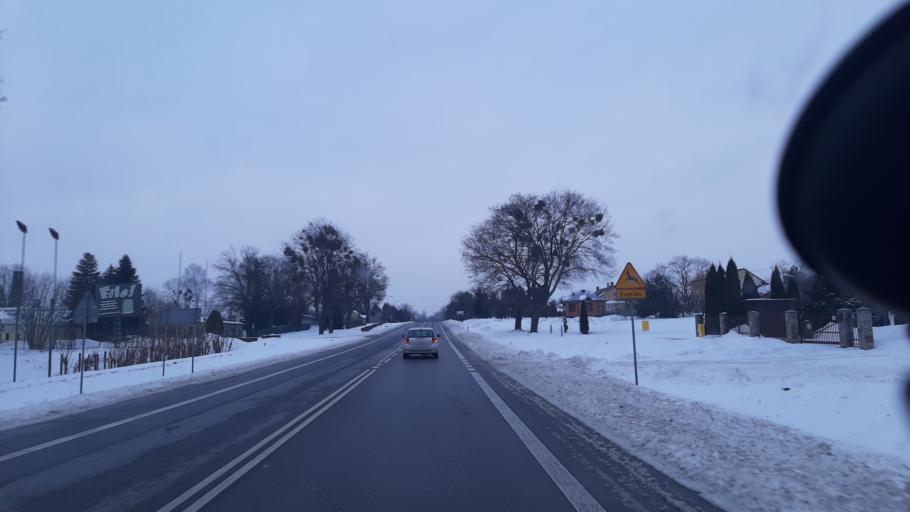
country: PL
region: Lublin Voivodeship
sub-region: Powiat lubelski
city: Garbow
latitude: 51.3585
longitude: 22.3178
